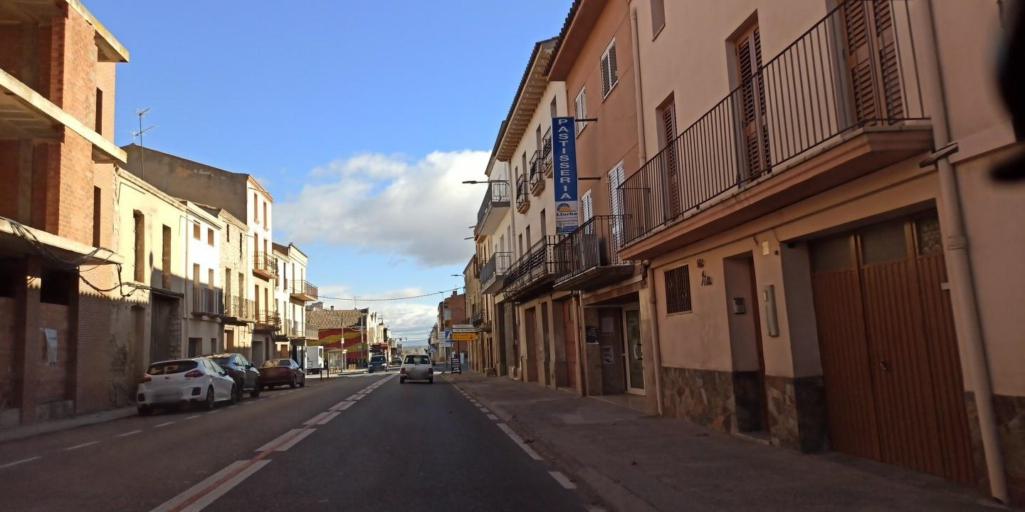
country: ES
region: Catalonia
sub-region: Provincia de Lleida
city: Bellcaire d'Urgell
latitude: 41.7586
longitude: 0.9037
